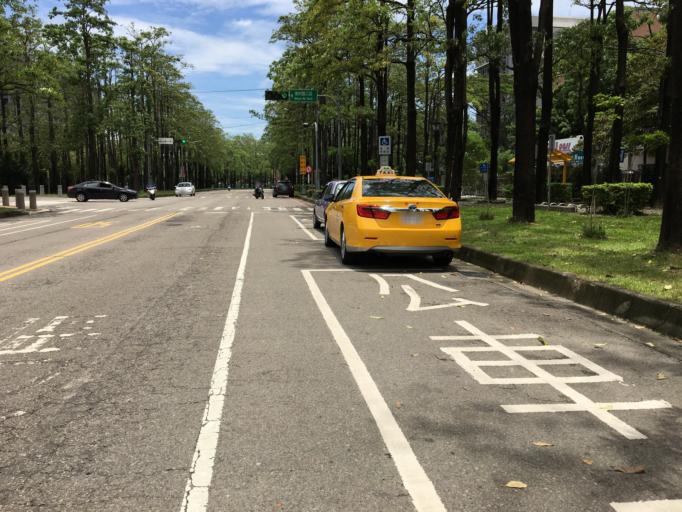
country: TW
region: Taiwan
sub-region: Taichung City
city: Taichung
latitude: 24.1219
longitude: 120.6719
